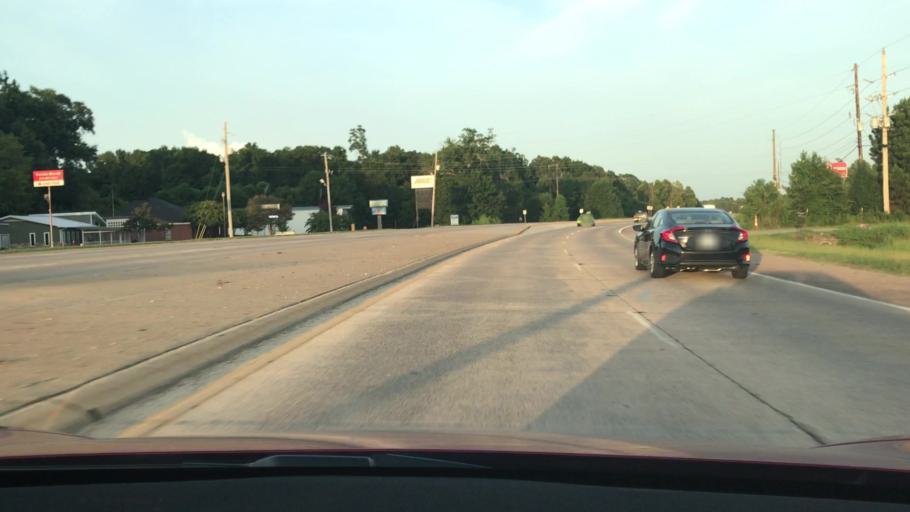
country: US
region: Louisiana
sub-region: Bossier Parish
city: Bossier City
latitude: 32.4014
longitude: -93.7768
